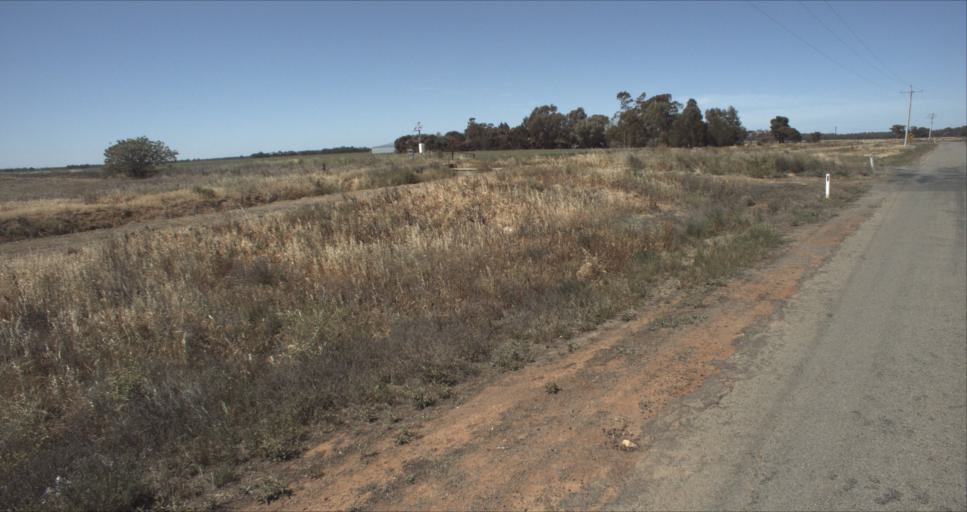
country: AU
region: New South Wales
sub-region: Leeton
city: Leeton
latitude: -34.5812
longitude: 146.3087
